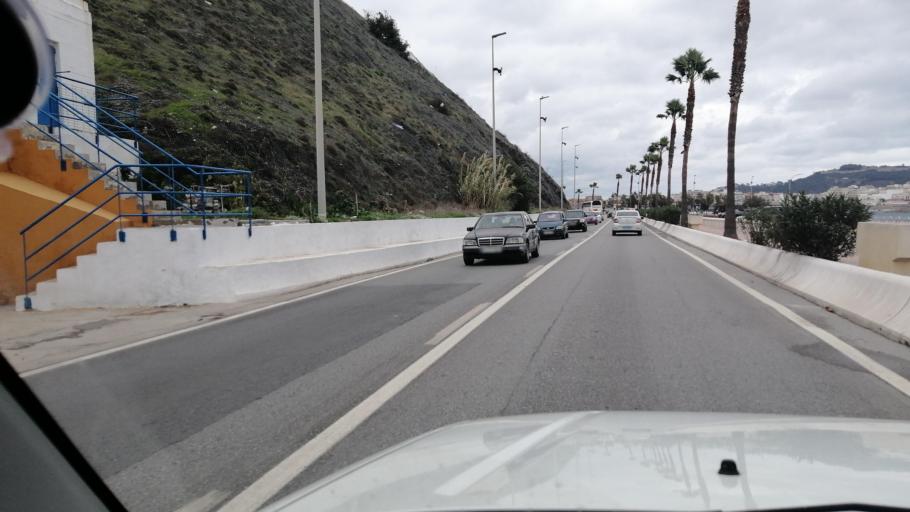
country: ES
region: Ceuta
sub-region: Ceuta
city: Ceuta
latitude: 35.8807
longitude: -5.3266
